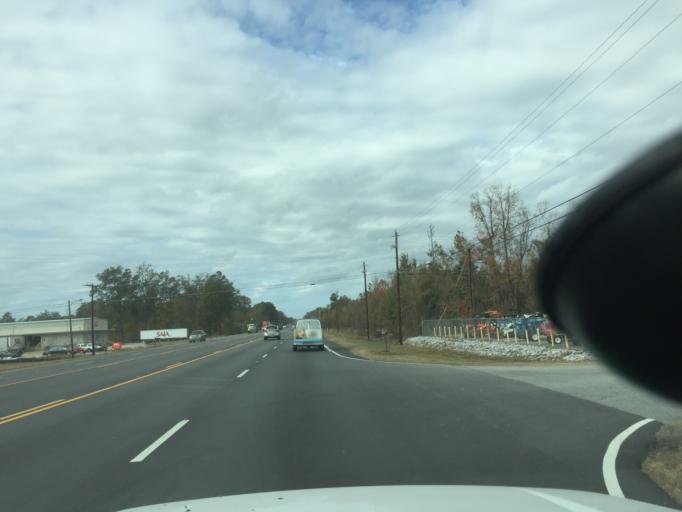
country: US
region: Georgia
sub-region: Chatham County
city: Garden City
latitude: 32.0899
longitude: -81.1838
